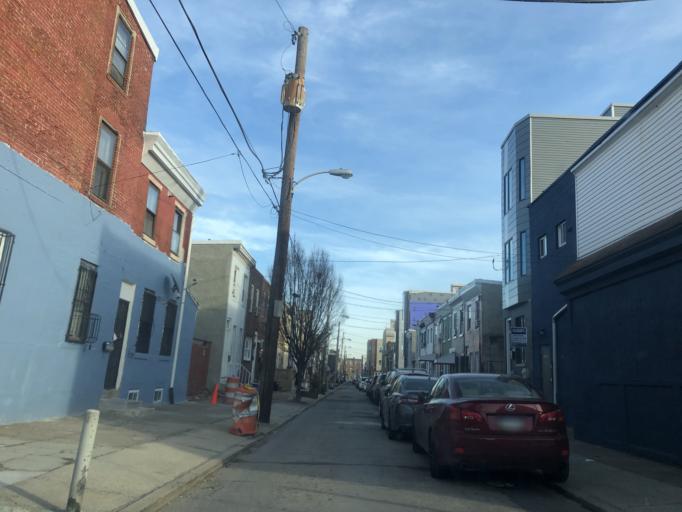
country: US
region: Pennsylvania
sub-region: Philadelphia County
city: Philadelphia
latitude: 39.9267
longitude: -75.1557
